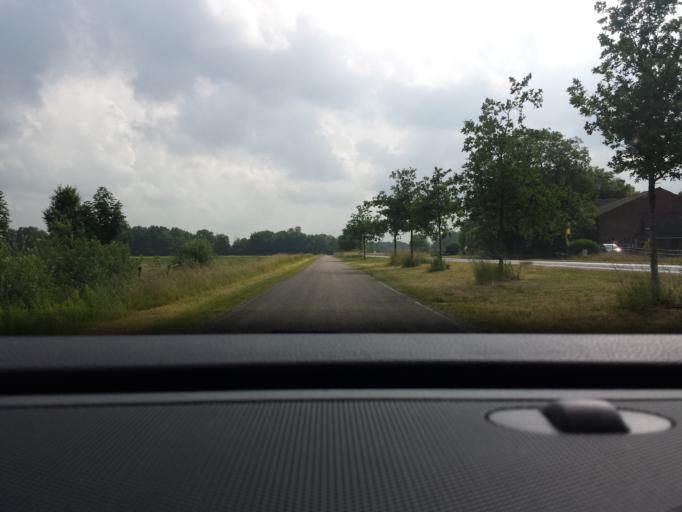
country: NL
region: Gelderland
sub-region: Berkelland
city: Borculo
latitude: 52.0963
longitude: 6.4837
